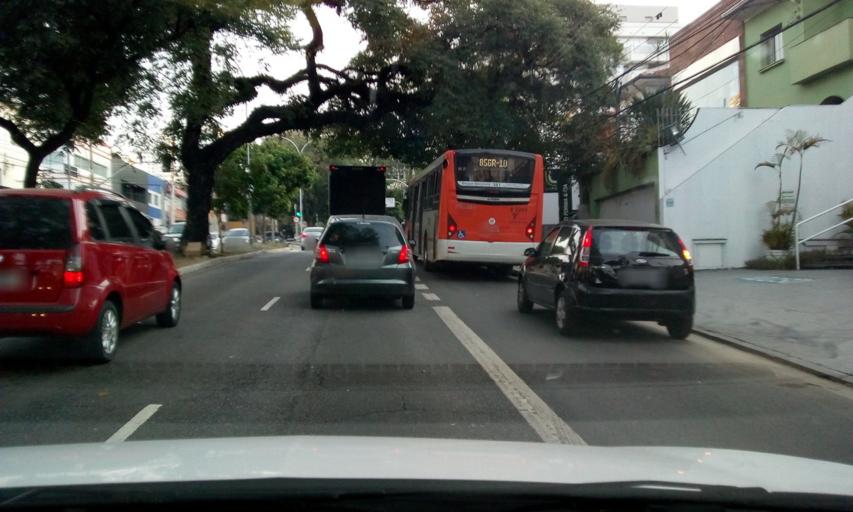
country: BR
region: Sao Paulo
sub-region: Sao Paulo
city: Sao Paulo
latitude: -23.5296
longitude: -46.6846
